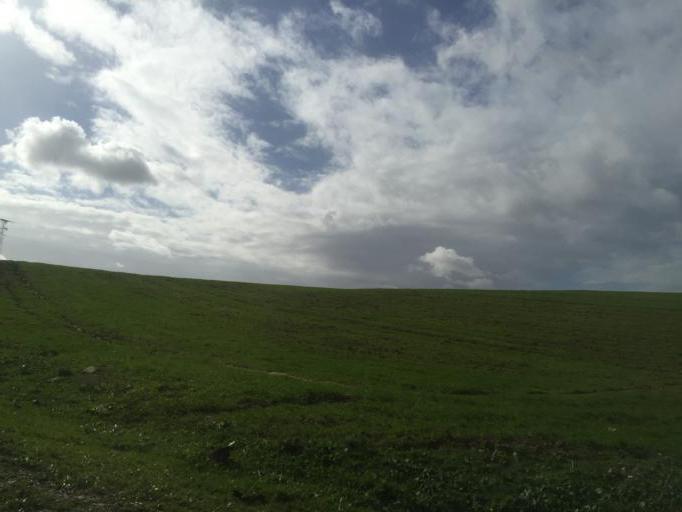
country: TN
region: Nabul
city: El Mida
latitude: 36.8083
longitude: 10.8457
